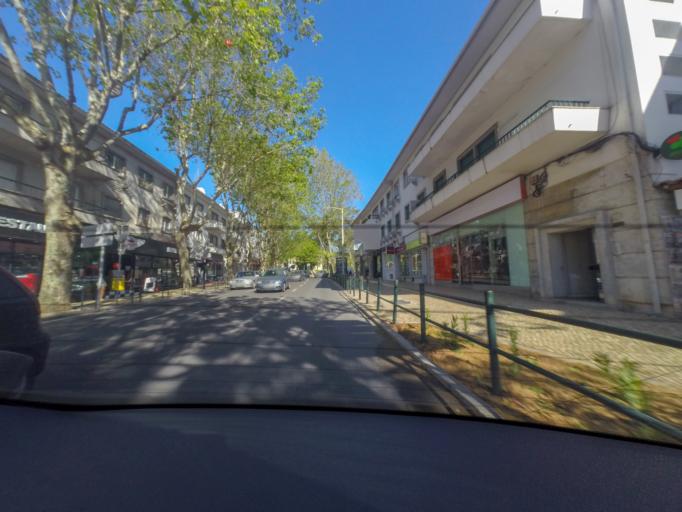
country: PT
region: Lisbon
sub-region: Cascais
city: Cascais
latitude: 38.7009
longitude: -9.4209
